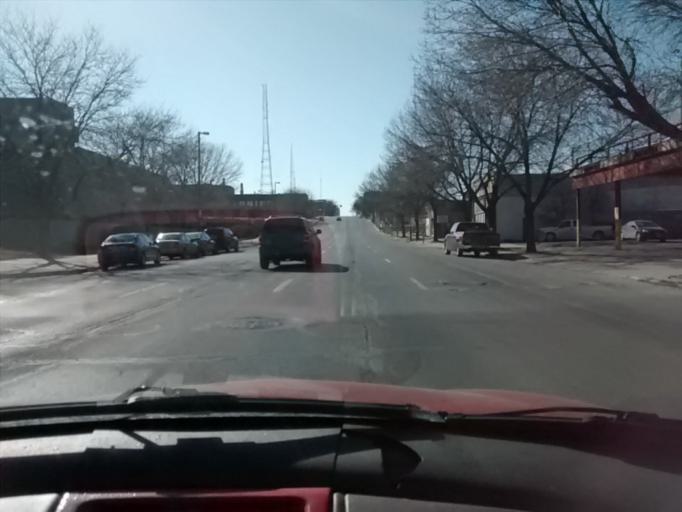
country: US
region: Nebraska
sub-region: Douglas County
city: Omaha
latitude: 41.2576
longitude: -95.9437
